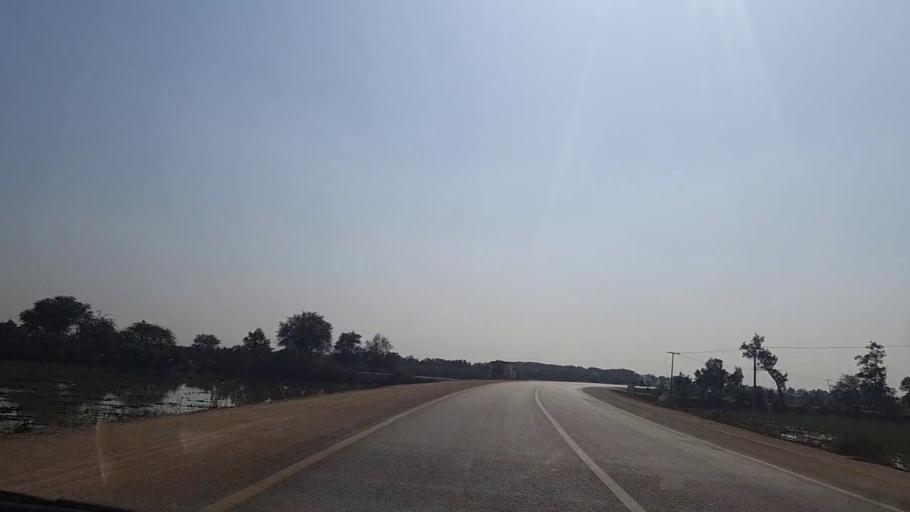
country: PK
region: Sindh
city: Sakrand
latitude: 25.9989
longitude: 68.3936
